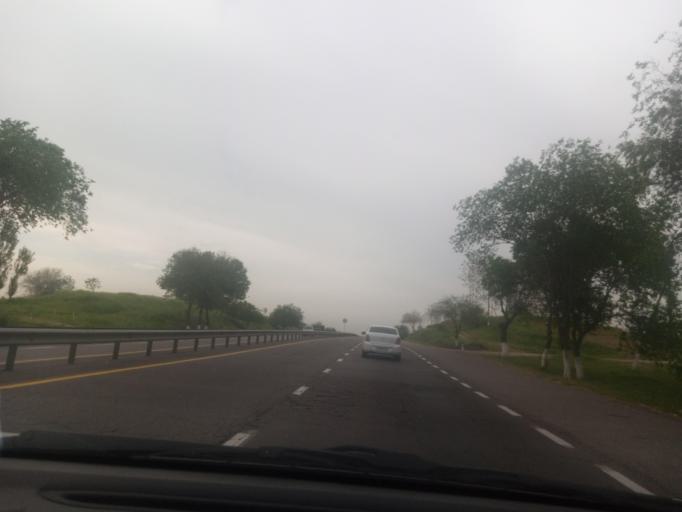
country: UZ
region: Toshkent
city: Tuytepa
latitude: 41.0839
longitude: 69.4676
